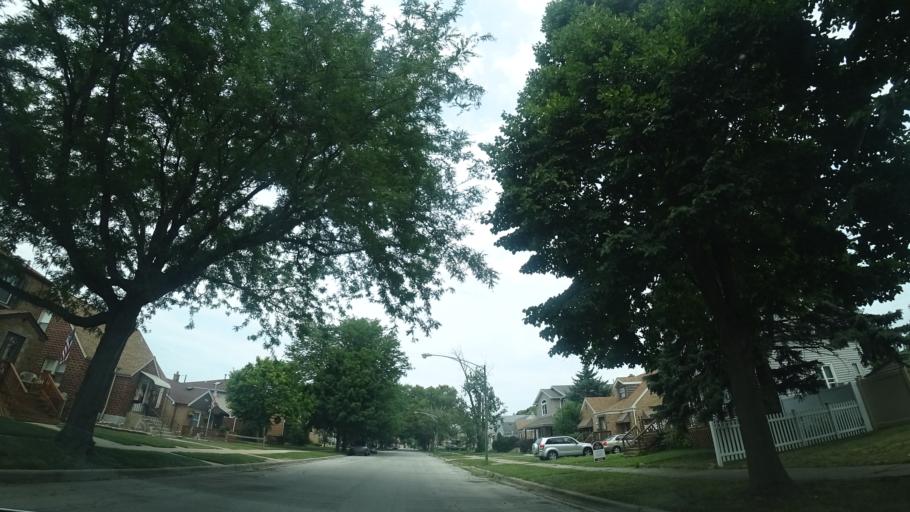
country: US
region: Illinois
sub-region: Cook County
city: Merrionette Park
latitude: 41.6970
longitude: -87.7144
